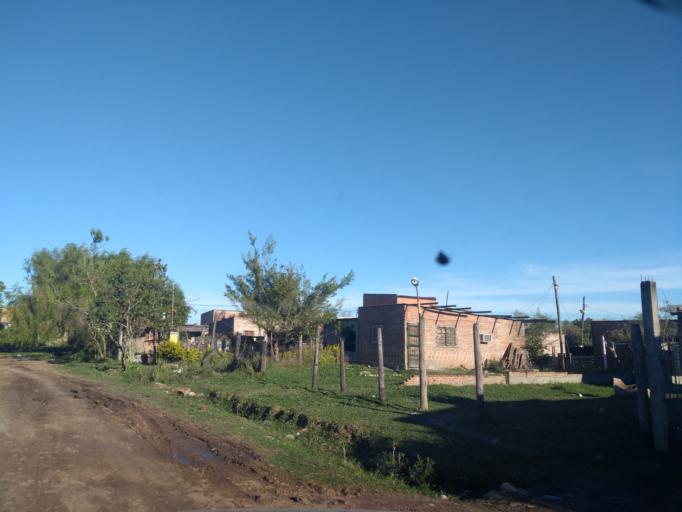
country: AR
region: Chaco
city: Barranqueras
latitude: -27.4723
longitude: -58.9273
